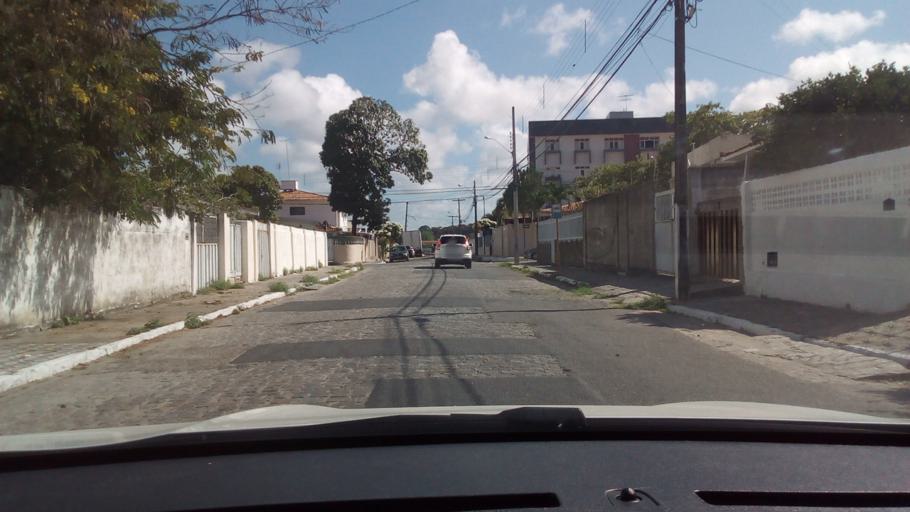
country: BR
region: Paraiba
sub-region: Joao Pessoa
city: Joao Pessoa
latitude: -7.1229
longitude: -34.8387
